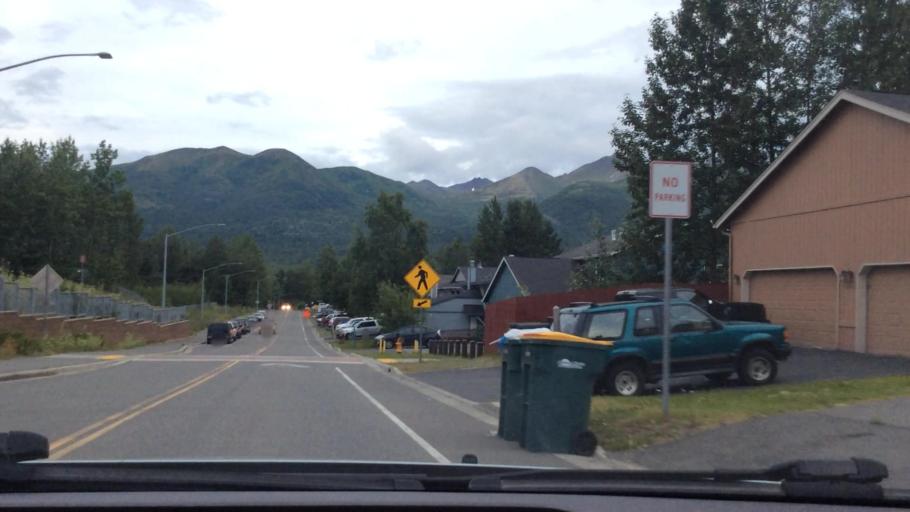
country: US
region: Alaska
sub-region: Anchorage Municipality
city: Elmendorf Air Force Base
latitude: 61.1919
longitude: -149.7303
